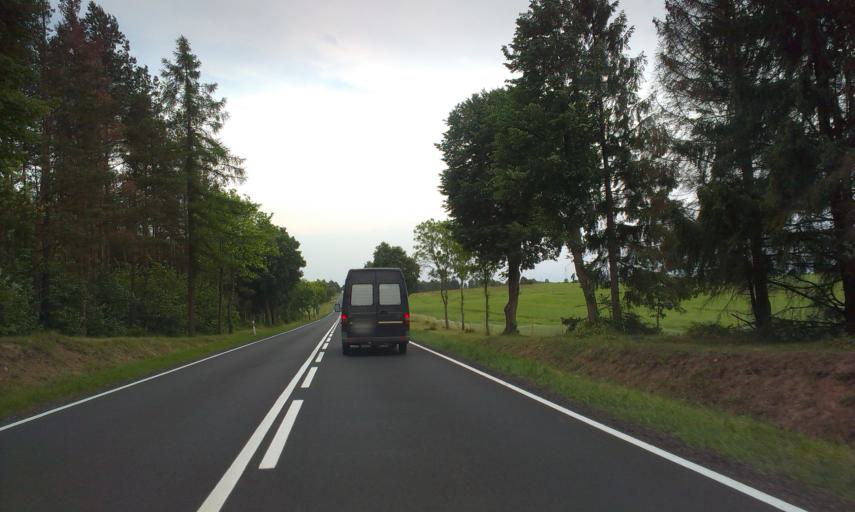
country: PL
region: West Pomeranian Voivodeship
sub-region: Powiat szczecinecki
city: Szczecinek
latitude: 53.7826
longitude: 16.6410
